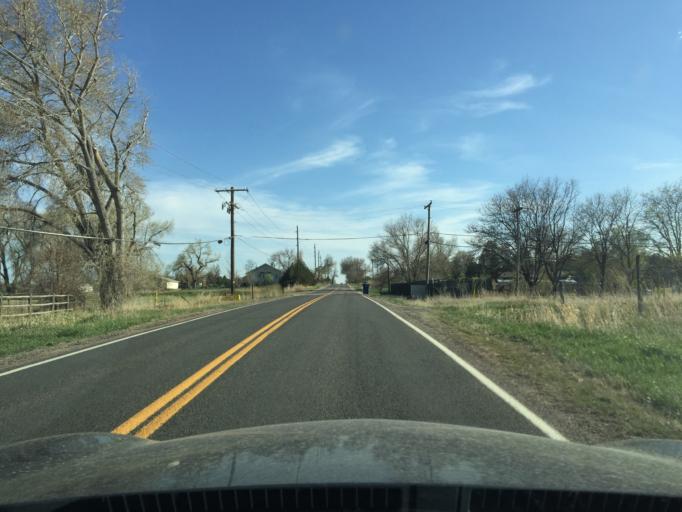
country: US
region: Colorado
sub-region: Boulder County
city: Erie
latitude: 40.0483
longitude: -105.0745
